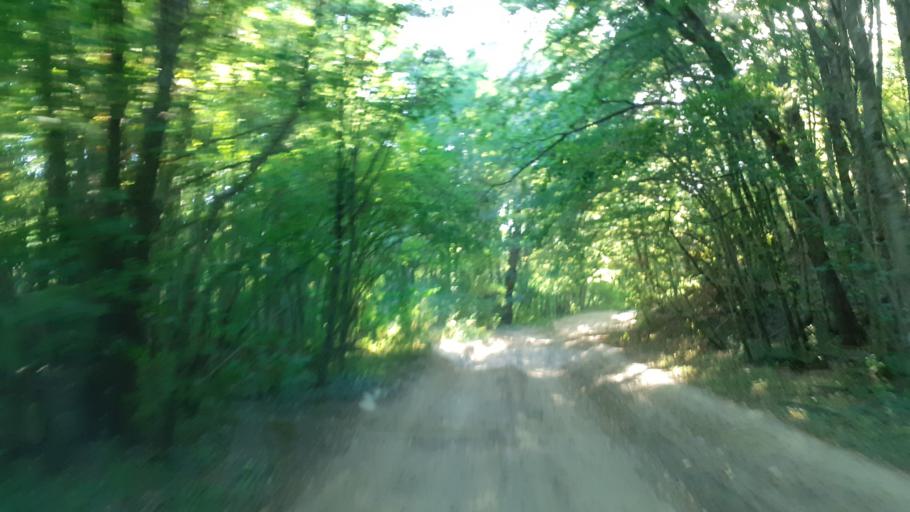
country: RU
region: Krasnodarskiy
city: Azovskaya
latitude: 44.6643
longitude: 38.4961
